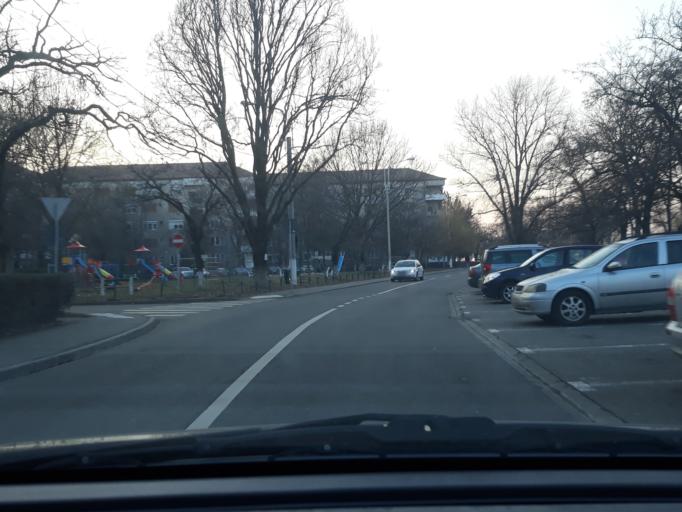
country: RO
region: Bihor
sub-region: Comuna Biharea
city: Oradea
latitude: 47.0655
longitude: 21.9144
